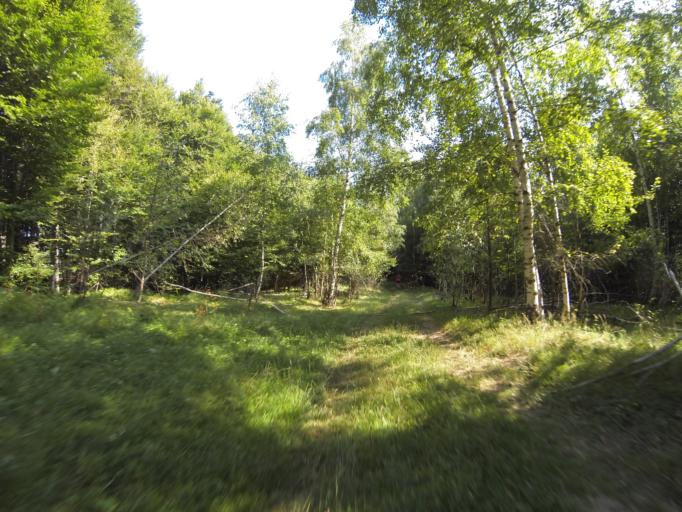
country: RO
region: Valcea
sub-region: Comuna Vaideeni
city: Vaideeni
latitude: 45.2244
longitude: 23.9677
